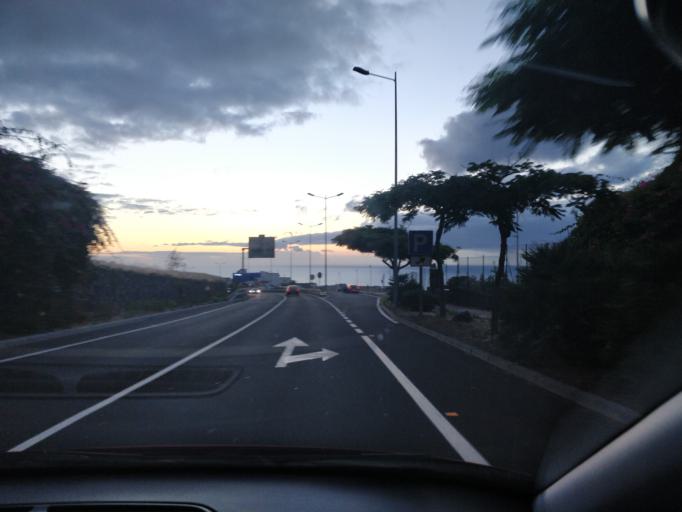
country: ES
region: Canary Islands
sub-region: Provincia de Santa Cruz de Tenerife
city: La Orotava
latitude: 28.4040
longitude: -16.5180
